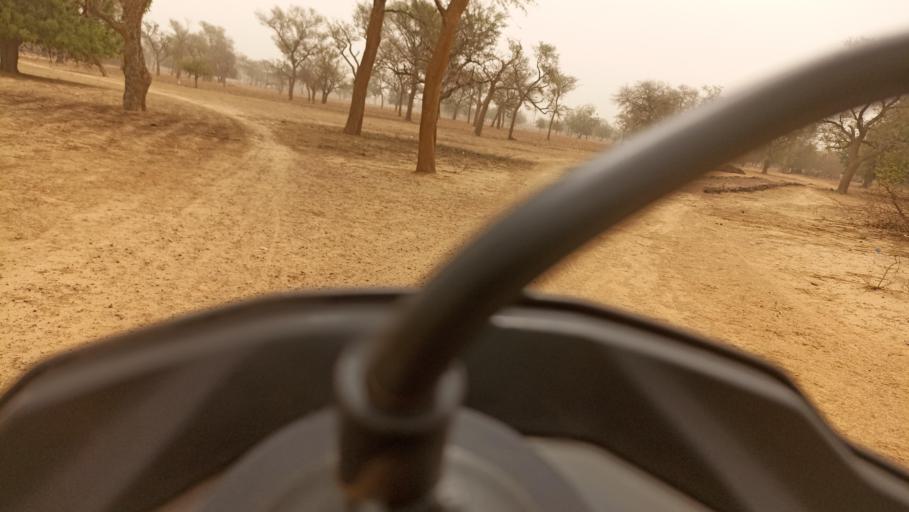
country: BF
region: Nord
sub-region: Province du Zondoma
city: Gourcy
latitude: 13.2495
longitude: -2.5973
